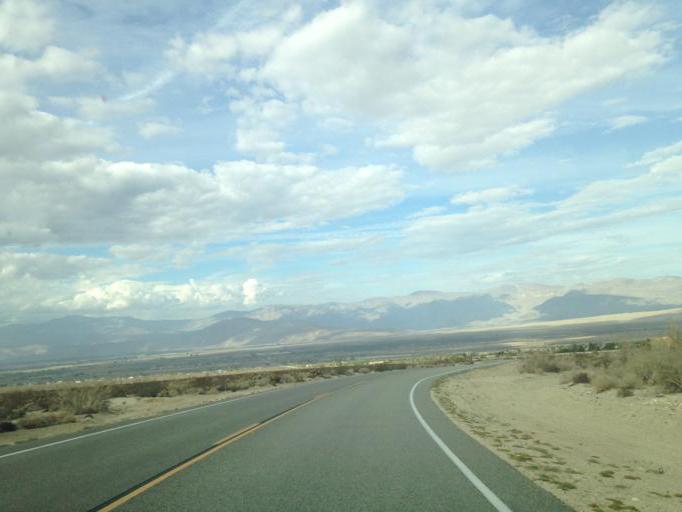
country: US
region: California
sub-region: San Diego County
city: Borrego Springs
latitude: 33.1810
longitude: -116.3324
